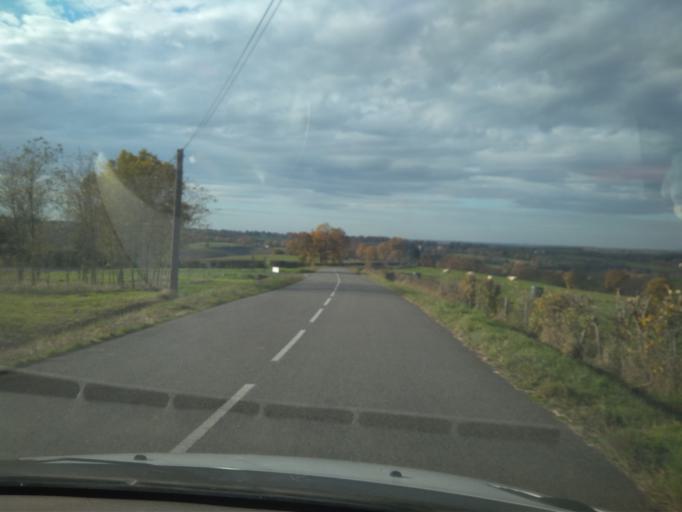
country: FR
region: Auvergne
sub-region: Departement de l'Allier
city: Lapalisse
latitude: 46.1760
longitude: 3.6835
